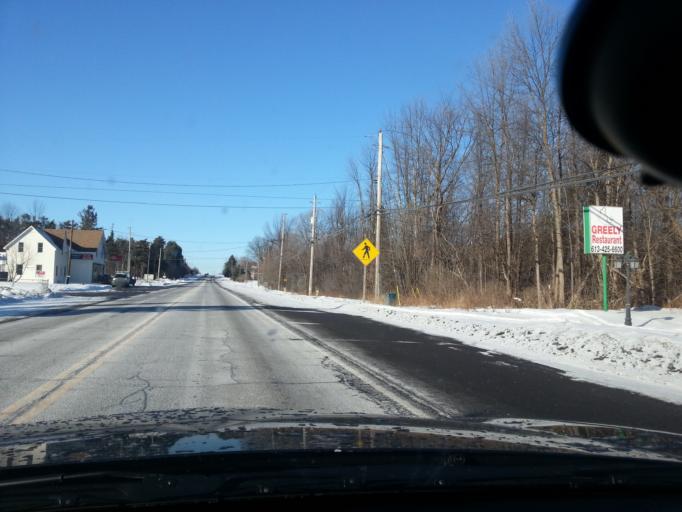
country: CA
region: Ontario
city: Ottawa
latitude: 45.2852
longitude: -75.5733
